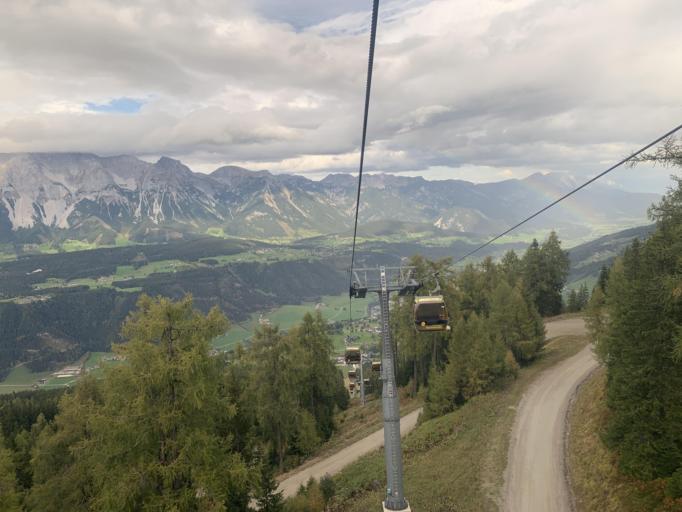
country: AT
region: Styria
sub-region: Politischer Bezirk Liezen
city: Schladming
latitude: 47.3635
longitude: 13.6422
